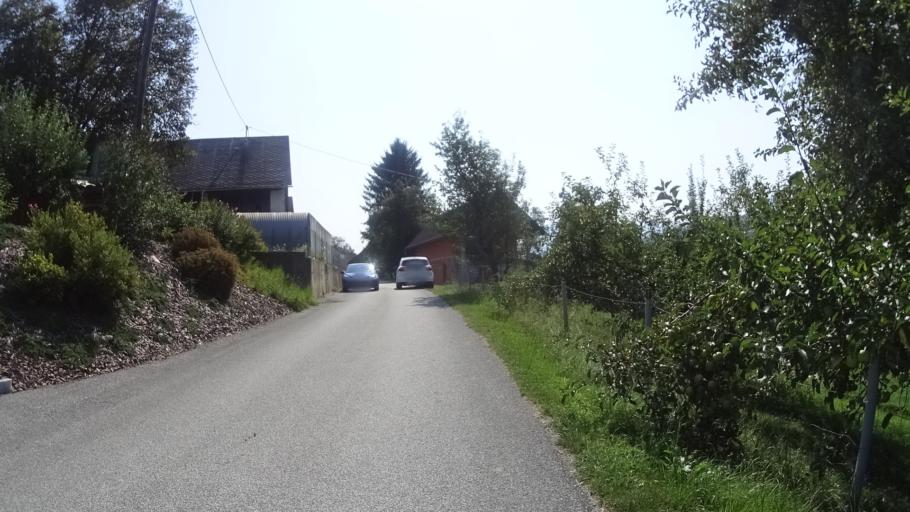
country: AT
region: Carinthia
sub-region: Politischer Bezirk Volkermarkt
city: Gallizien
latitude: 46.5705
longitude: 14.5145
